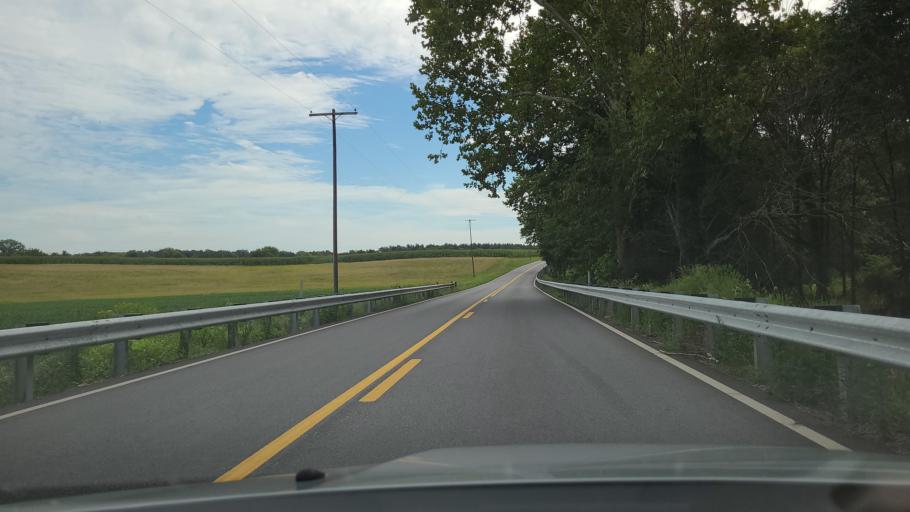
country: US
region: Maryland
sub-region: Frederick County
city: Thurmont
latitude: 39.6135
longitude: -77.3589
